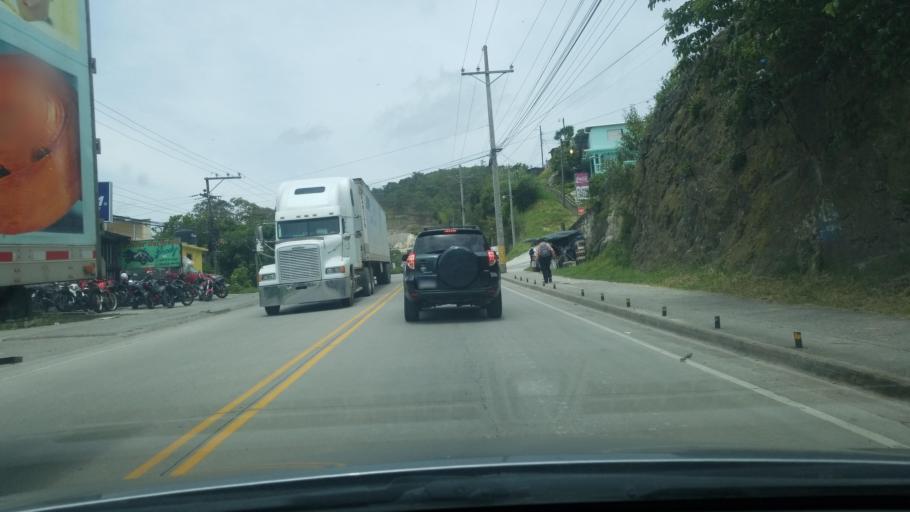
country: HN
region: Copan
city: Santa Rosa de Copan
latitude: 14.7609
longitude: -88.7753
